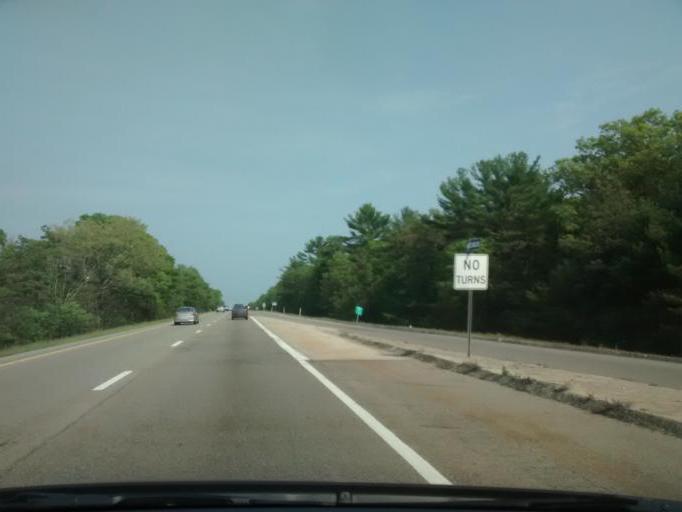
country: US
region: Massachusetts
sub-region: Plymouth County
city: Wareham Center
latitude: 41.7827
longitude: -70.7290
